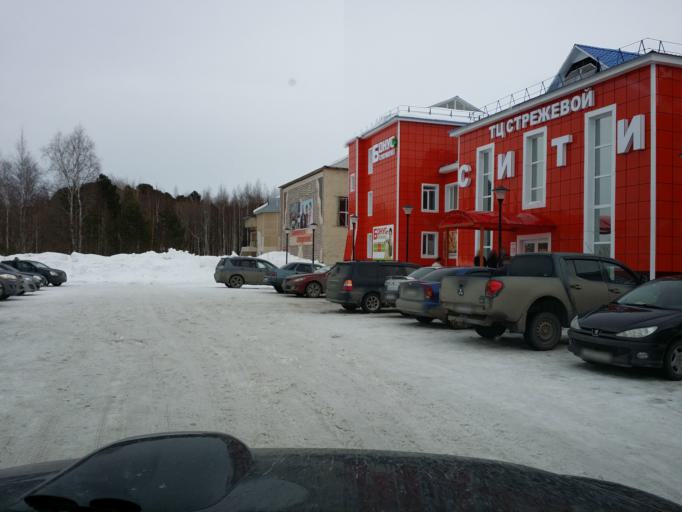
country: RU
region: Tomsk
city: Strezhevoy
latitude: 60.7253
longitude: 77.5976
